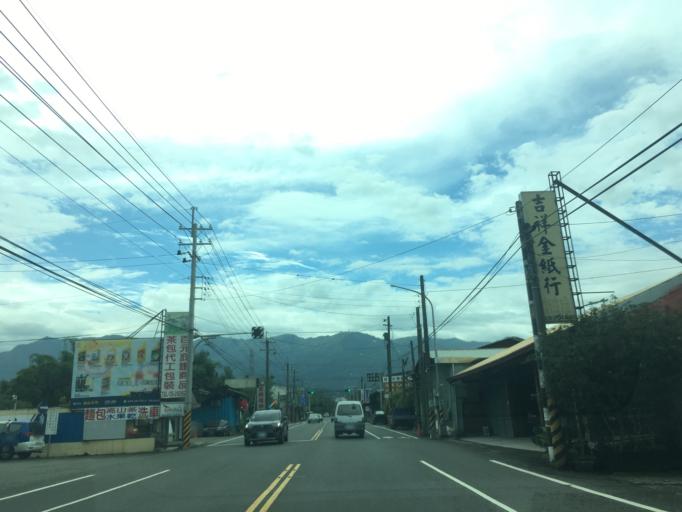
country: TW
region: Taiwan
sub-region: Yunlin
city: Douliu
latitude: 23.5897
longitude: 120.5448
